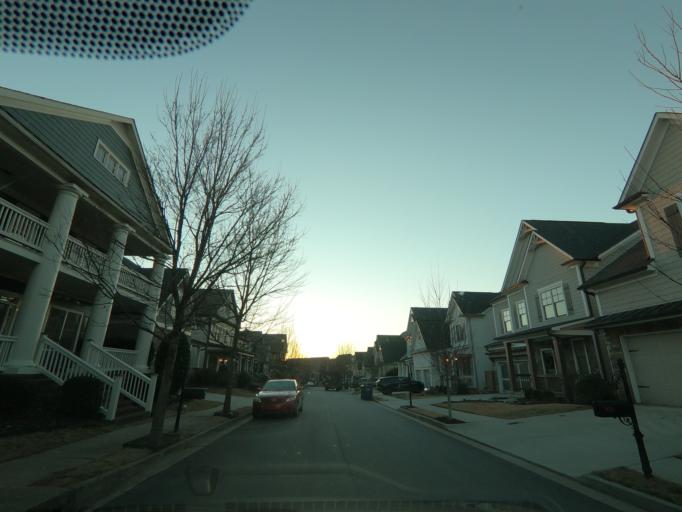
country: US
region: Georgia
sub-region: Cobb County
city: Vinings
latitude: 33.8102
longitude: -84.4508
